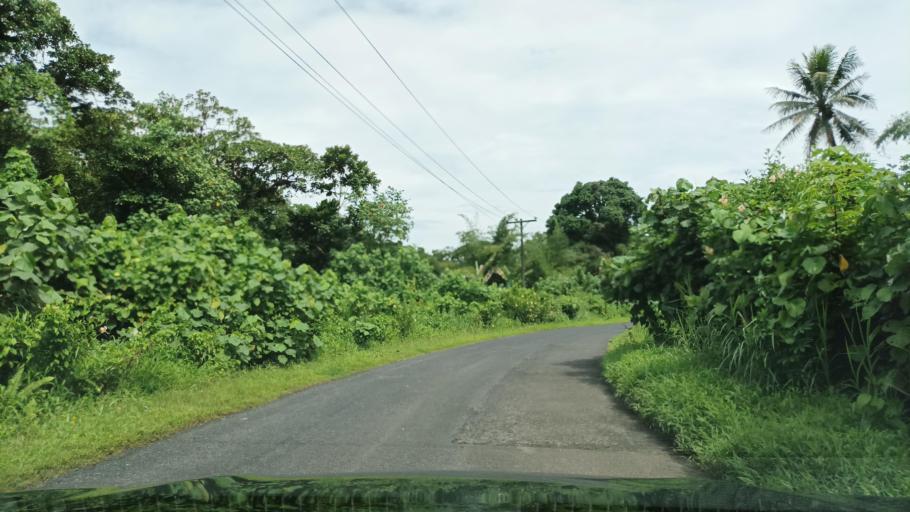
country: FM
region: Pohnpei
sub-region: Madolenihm Municipality
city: Madolenihm Municipality Government
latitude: 6.8689
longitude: 158.2877
